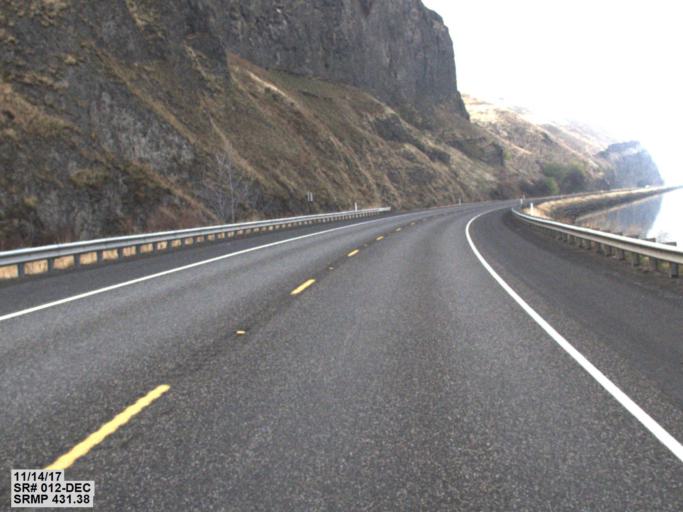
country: US
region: Washington
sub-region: Asotin County
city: Clarkston Heights-Vineland
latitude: 46.4147
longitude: -117.0926
